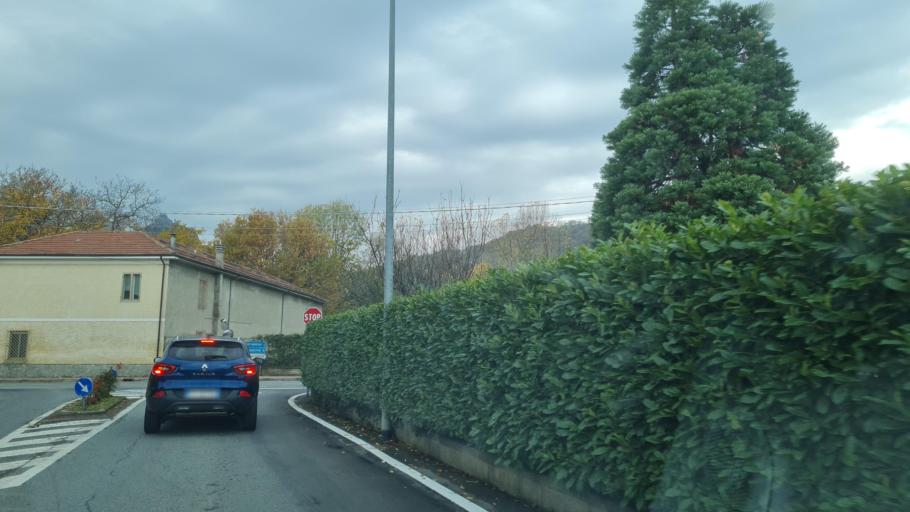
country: IT
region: Piedmont
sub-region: Provincia di Torino
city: Villar Dora
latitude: 45.1109
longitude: 7.3836
